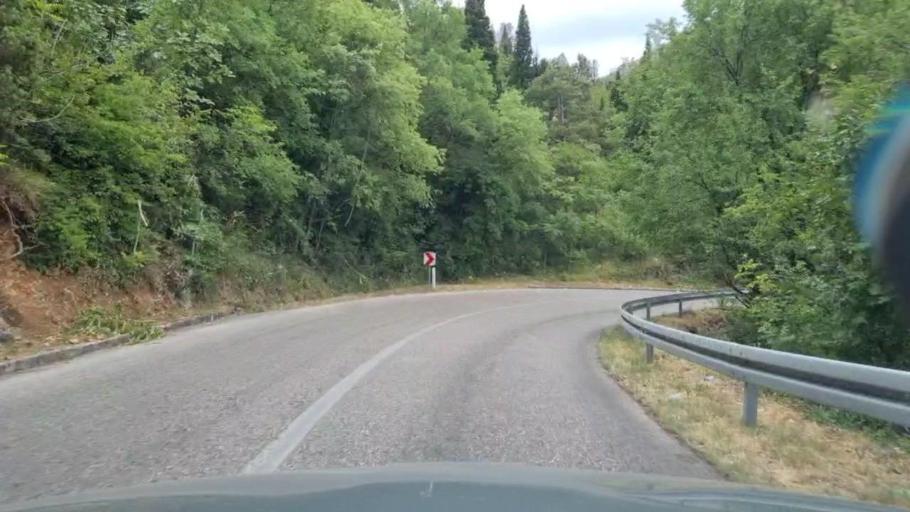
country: BA
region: Federation of Bosnia and Herzegovina
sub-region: Hercegovacko-Bosanski Kanton
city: Mostar
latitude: 43.3312
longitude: 17.7974
